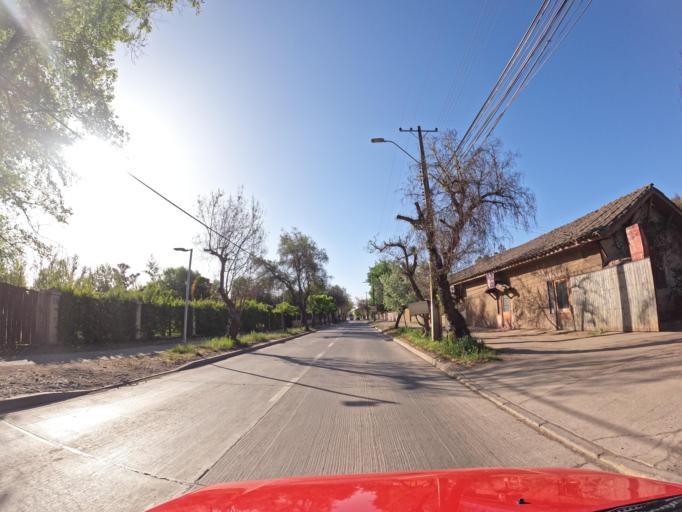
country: CL
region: O'Higgins
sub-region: Provincia de Colchagua
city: Santa Cruz
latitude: -34.7318
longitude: -71.2704
